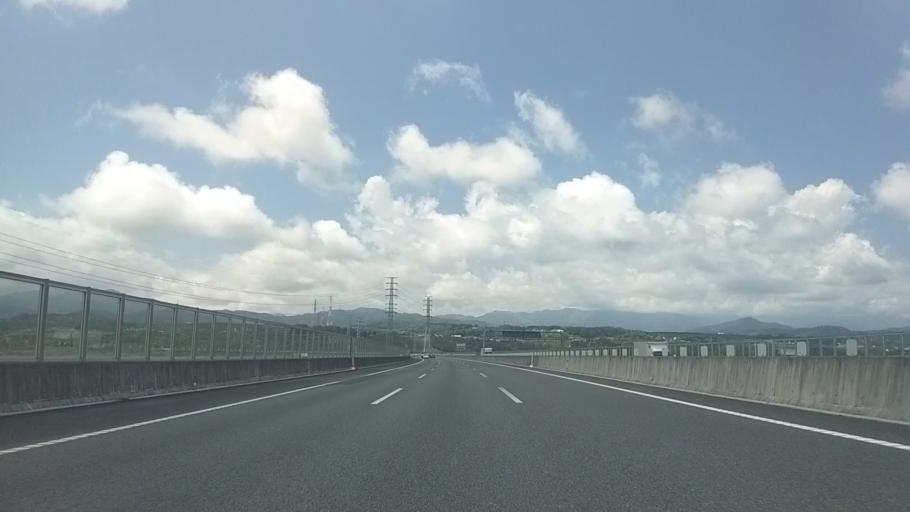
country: JP
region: Shizuoka
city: Fujinomiya
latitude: 35.2015
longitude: 138.6527
